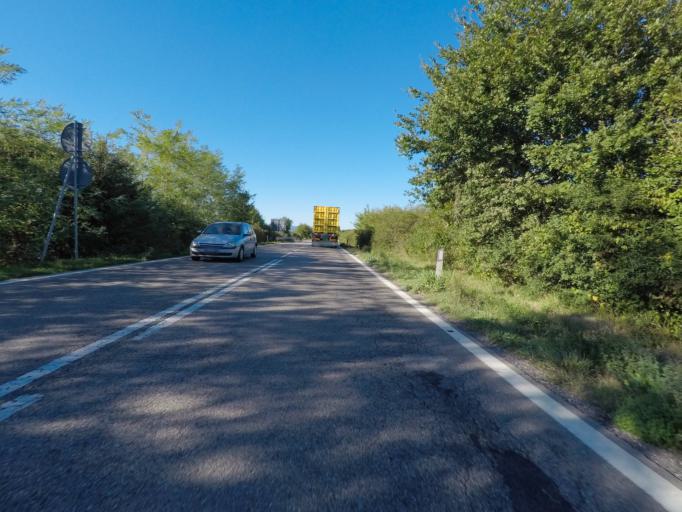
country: IT
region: Tuscany
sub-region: Provincia di Siena
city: Rosia
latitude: 43.2115
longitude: 11.2783
